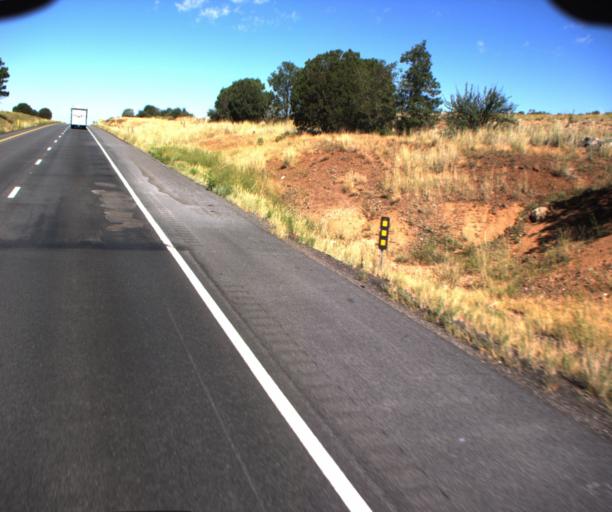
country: US
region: Arizona
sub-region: Coconino County
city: Williams
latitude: 35.2208
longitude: -112.3111
